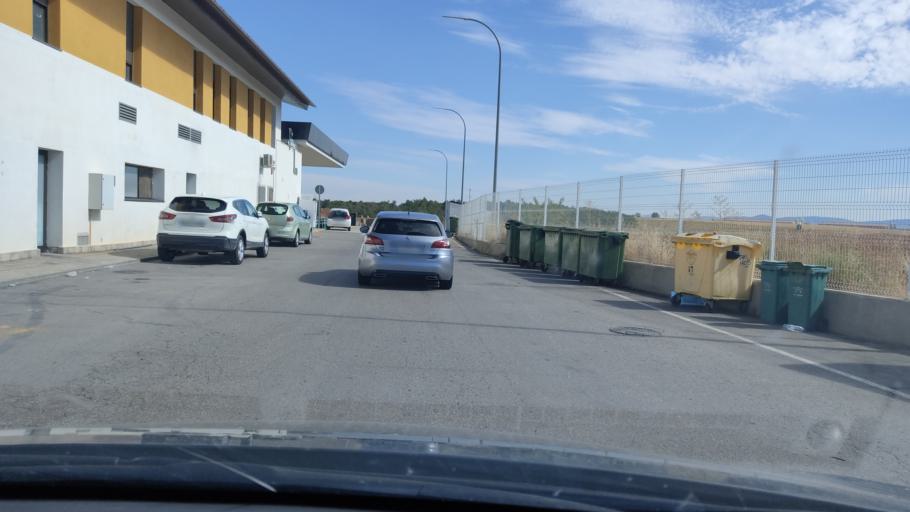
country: ES
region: Aragon
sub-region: Provincia de Zaragoza
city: Lechon
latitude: 41.0492
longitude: -1.2759
